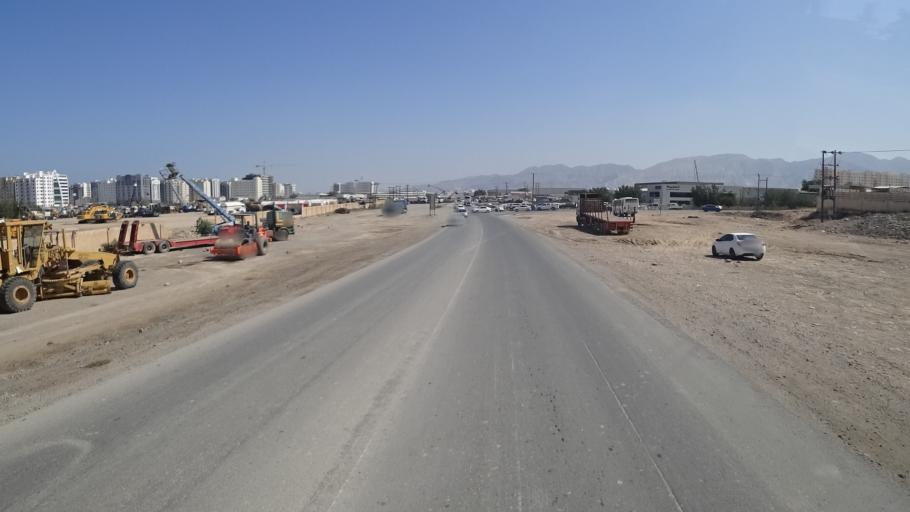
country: OM
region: Muhafazat Masqat
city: Bawshar
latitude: 23.5801
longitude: 58.3613
